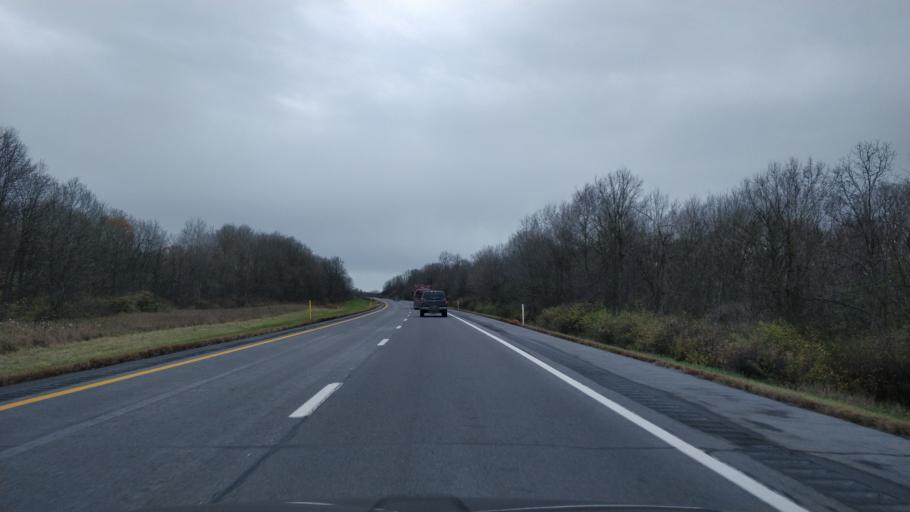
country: US
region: New York
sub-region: Jefferson County
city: Calcium
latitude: 44.1123
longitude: -75.8949
